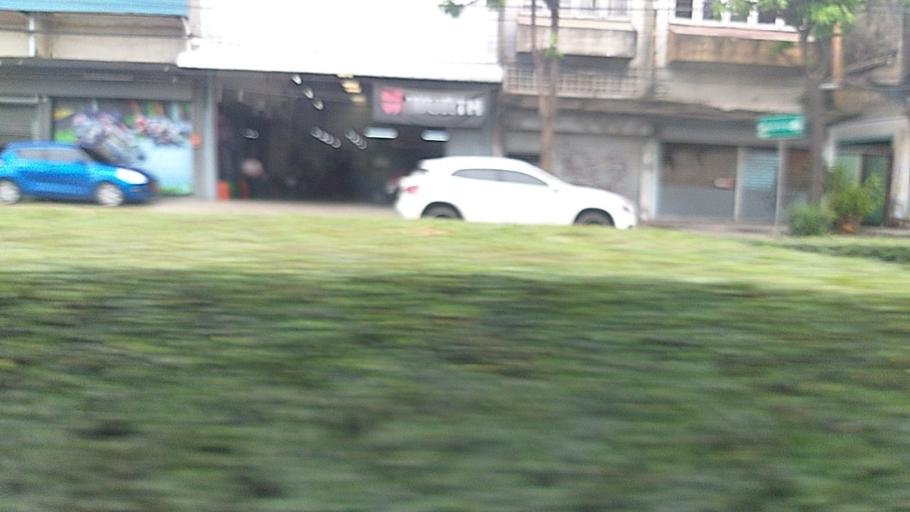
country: TH
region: Bangkok
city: Suan Luang
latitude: 13.7232
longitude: 100.6584
